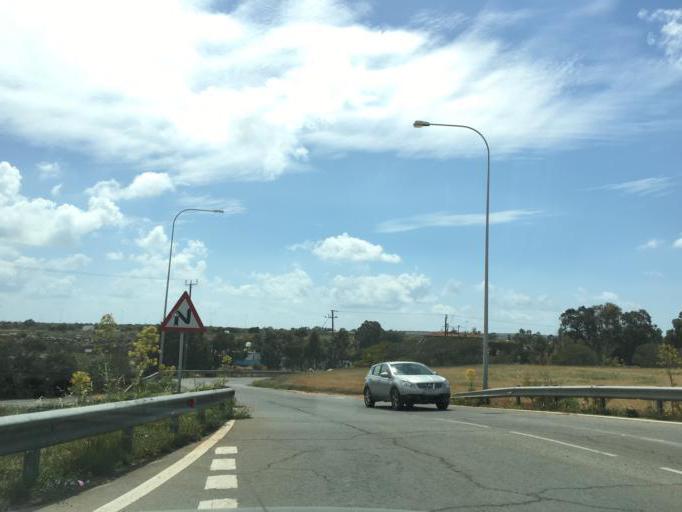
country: CY
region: Ammochostos
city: Liopetri
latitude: 34.9763
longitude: 33.8949
